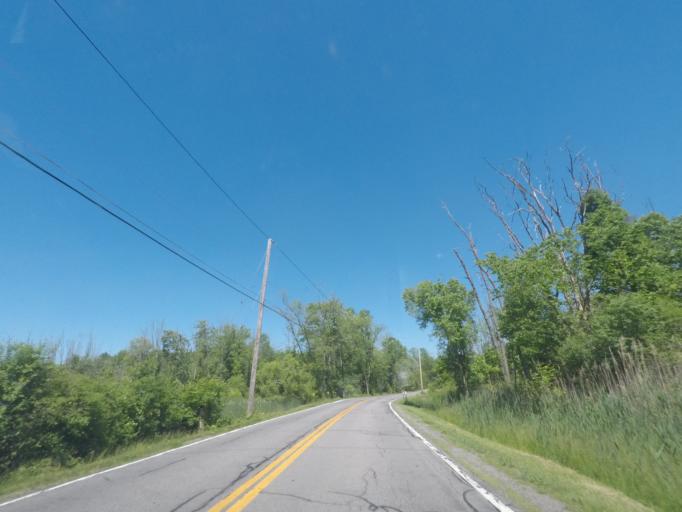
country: US
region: New York
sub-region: Saratoga County
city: Country Knolls
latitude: 42.8604
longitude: -73.8425
